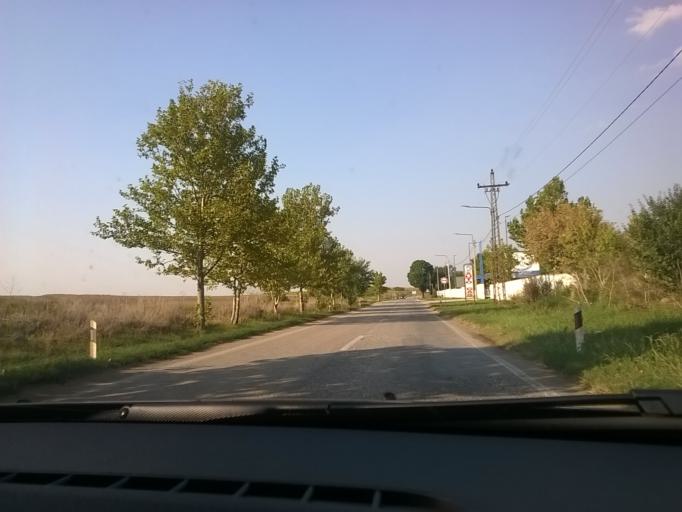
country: RS
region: Autonomna Pokrajina Vojvodina
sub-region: Juznobanatski Okrug
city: Vrsac
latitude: 45.1396
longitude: 21.2877
